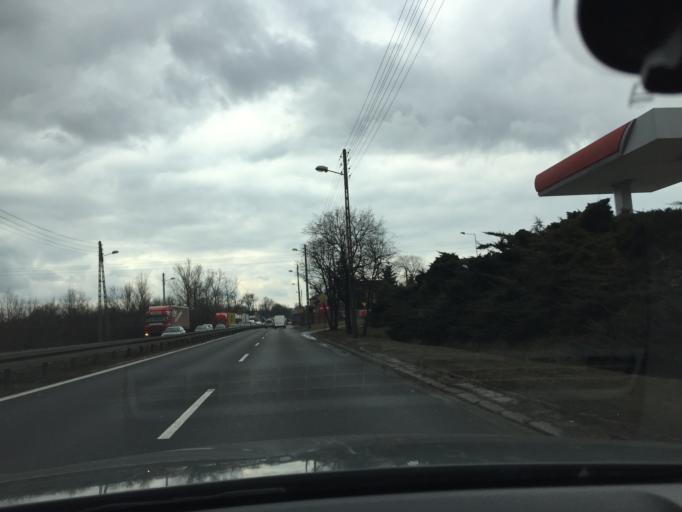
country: PL
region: Silesian Voivodeship
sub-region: Powiat czestochowski
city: Huta Stara B
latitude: 50.7582
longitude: 19.1582
